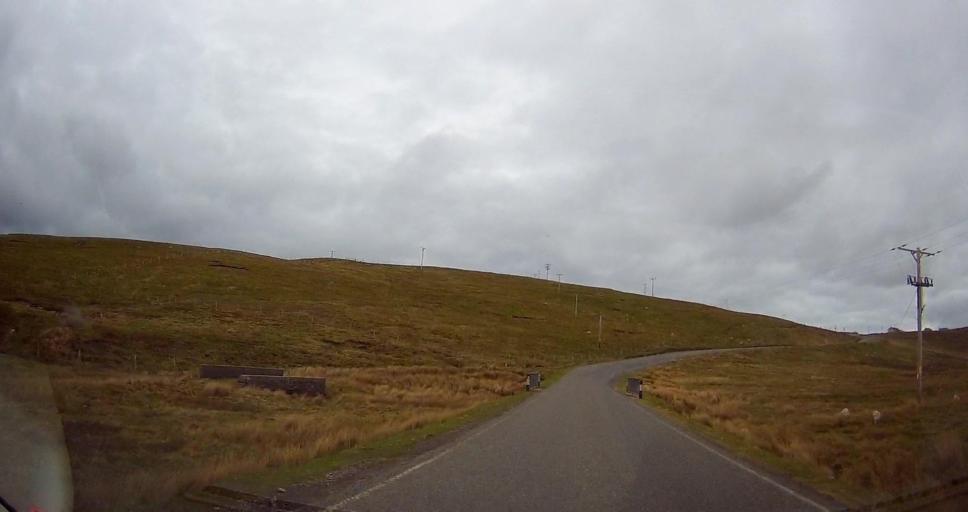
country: GB
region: Scotland
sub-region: Shetland Islands
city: Shetland
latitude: 60.6029
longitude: -1.0833
